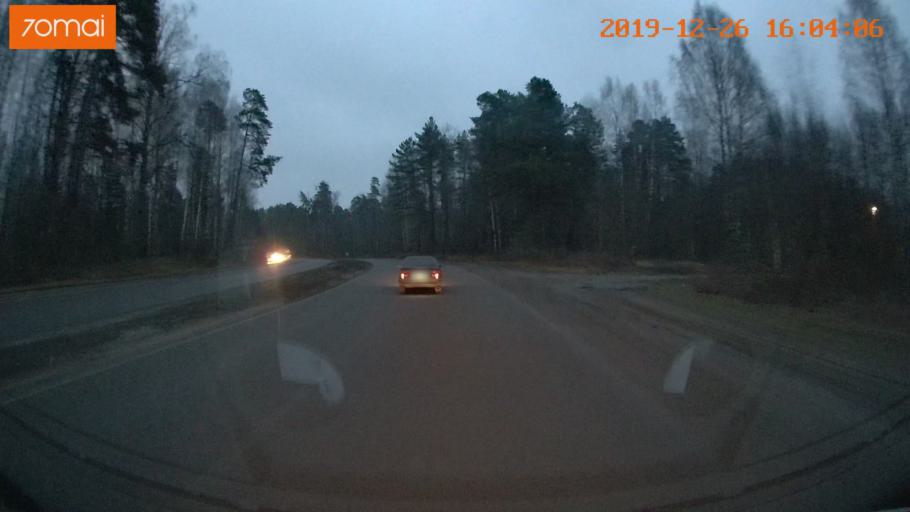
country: RU
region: Jaroslavl
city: Rybinsk
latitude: 58.0090
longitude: 38.8624
